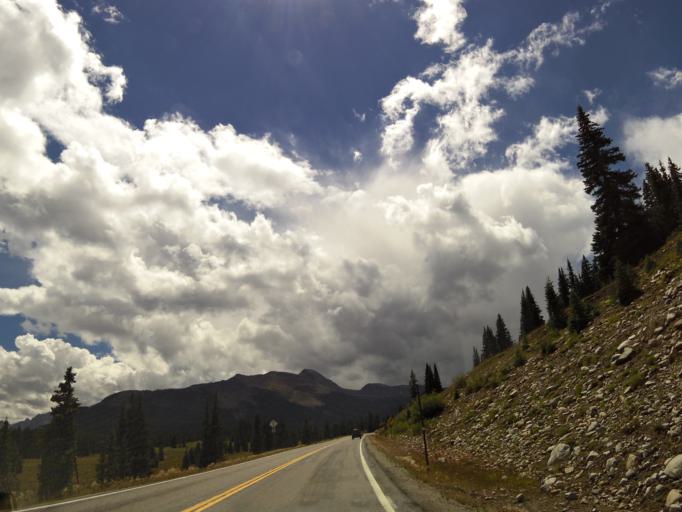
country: US
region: Colorado
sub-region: San Juan County
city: Silverton
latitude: 37.7574
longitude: -107.6805
